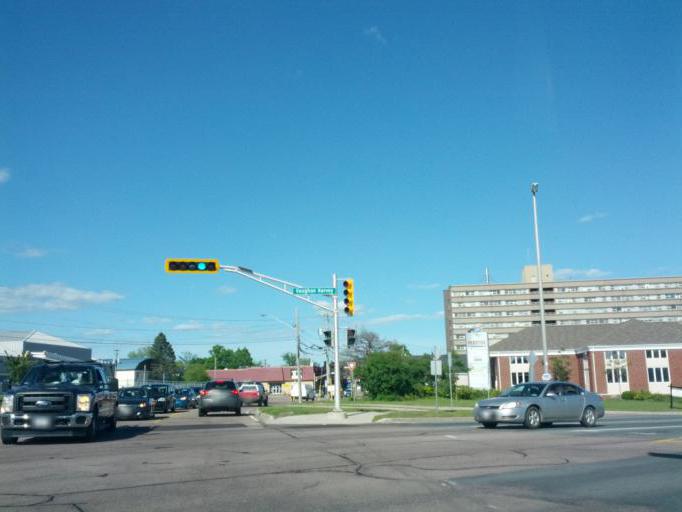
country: CA
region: New Brunswick
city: Moncton
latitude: 46.0883
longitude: -64.7957
